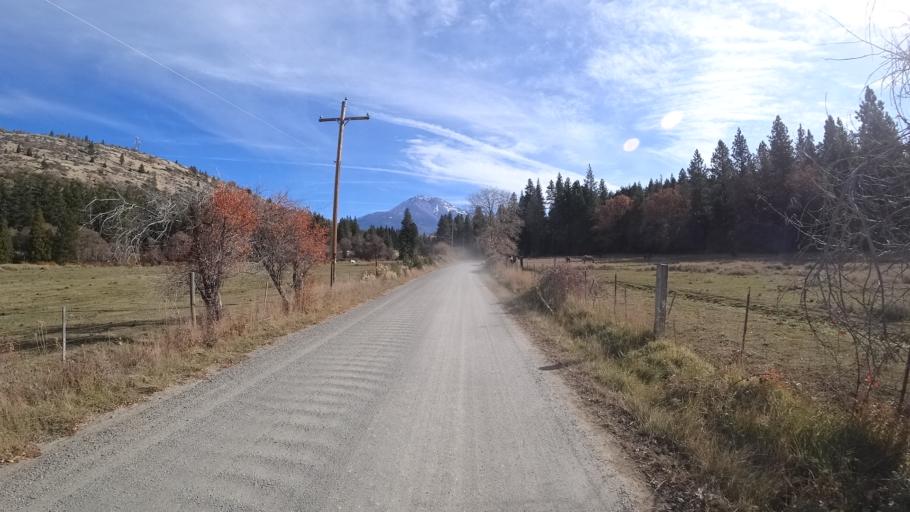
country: US
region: California
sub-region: Siskiyou County
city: Weed
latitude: 41.4317
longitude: -122.4040
